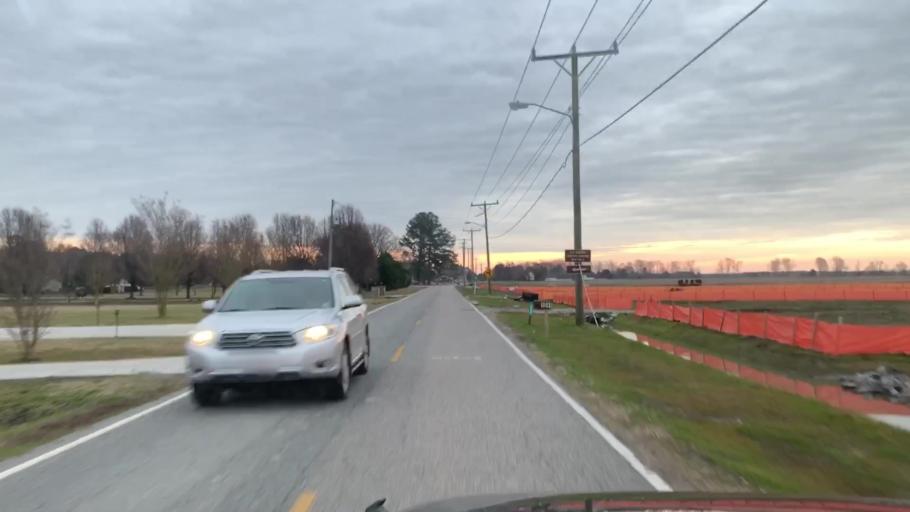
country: US
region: North Carolina
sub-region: Currituck County
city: Moyock
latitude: 36.6289
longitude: -76.1712
